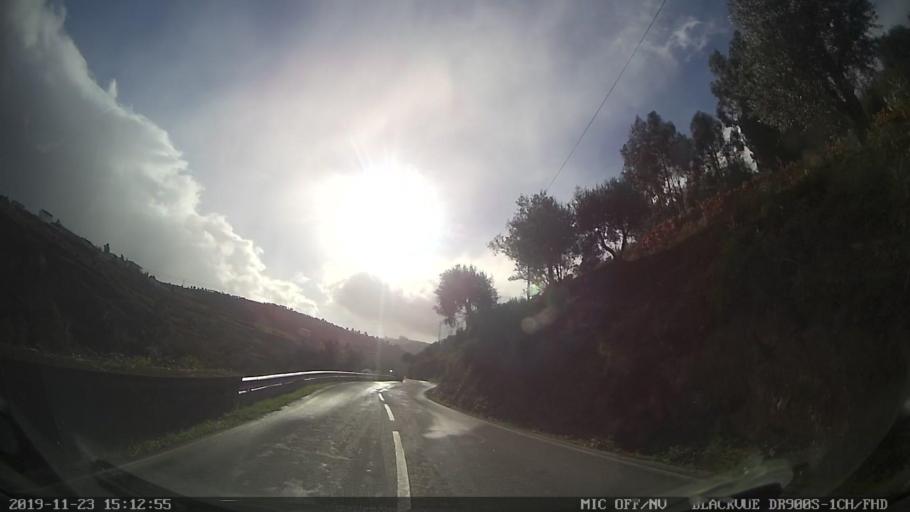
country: PT
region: Vila Real
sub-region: Peso da Regua
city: Peso da Regua
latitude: 41.1343
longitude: -7.7857
